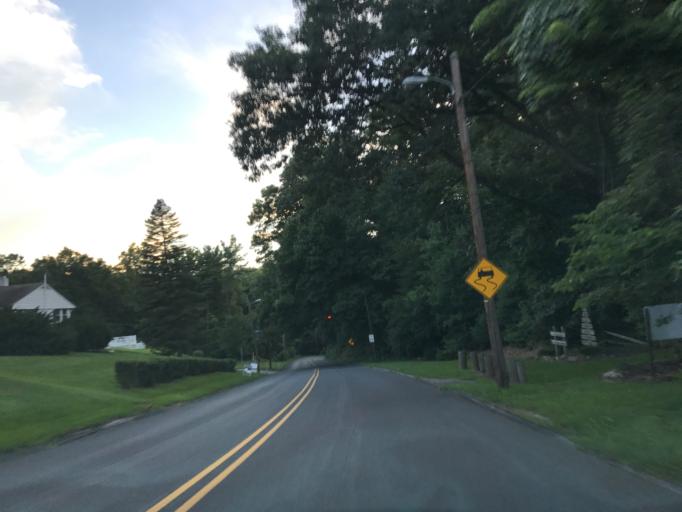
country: US
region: Pennsylvania
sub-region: York County
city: Valley View
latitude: 39.9494
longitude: -76.7015
